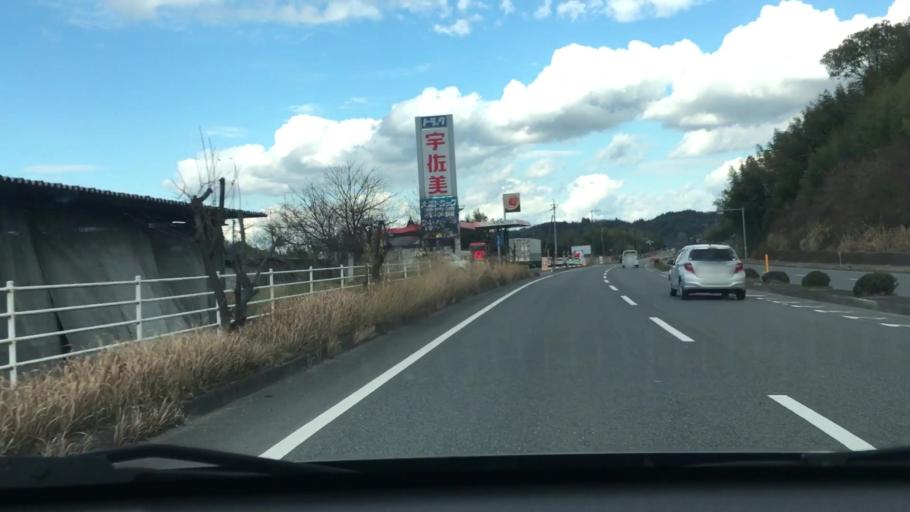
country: JP
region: Oita
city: Oita
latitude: 33.1244
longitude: 131.6548
